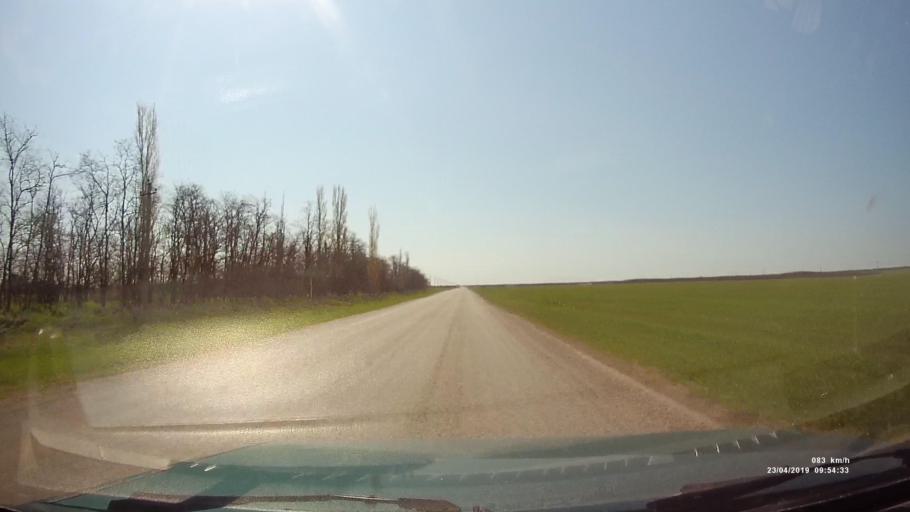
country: RU
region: Rostov
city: Orlovskiy
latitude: 46.8196
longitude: 42.0561
